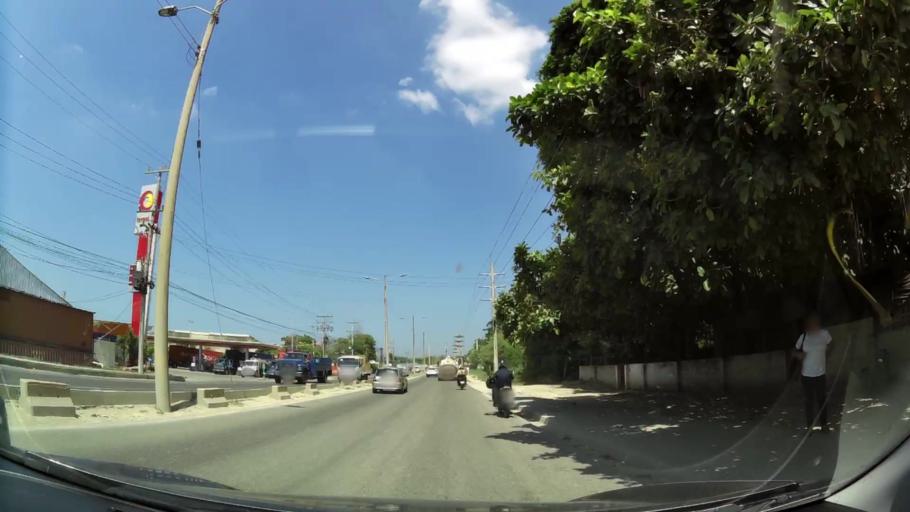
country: CO
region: Bolivar
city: Cartagena
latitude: 10.3647
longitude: -75.5078
